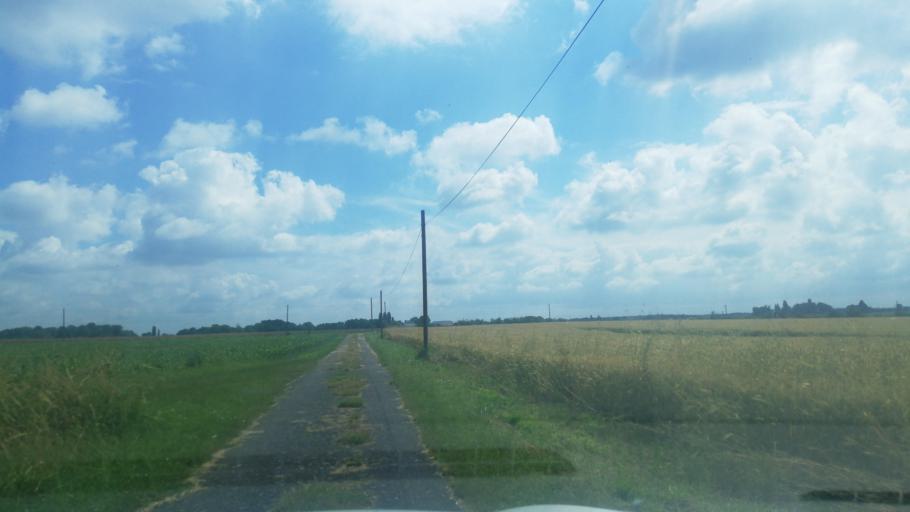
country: FR
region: Centre
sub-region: Departement du Loir-et-Cher
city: Saint-Romain-sur-Cher
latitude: 47.3751
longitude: 1.3846
